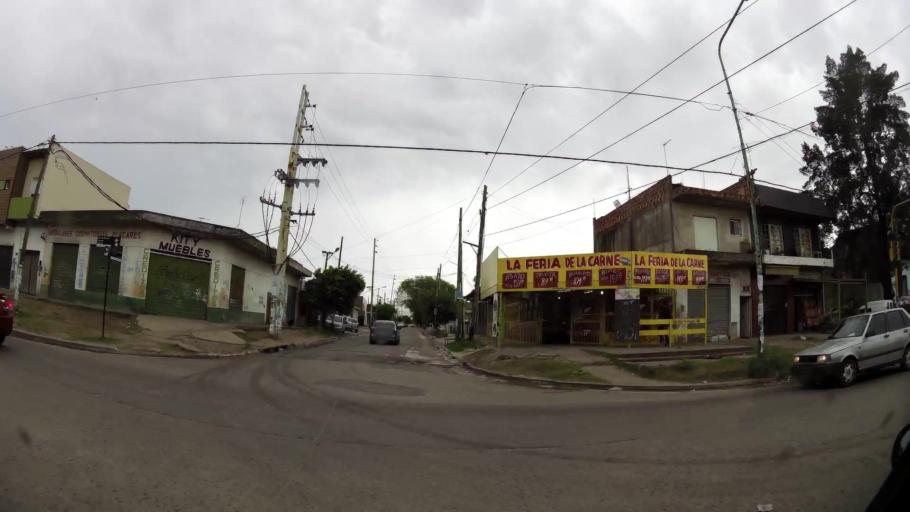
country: AR
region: Buenos Aires
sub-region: Partido de Quilmes
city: Quilmes
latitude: -34.7906
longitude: -58.2632
